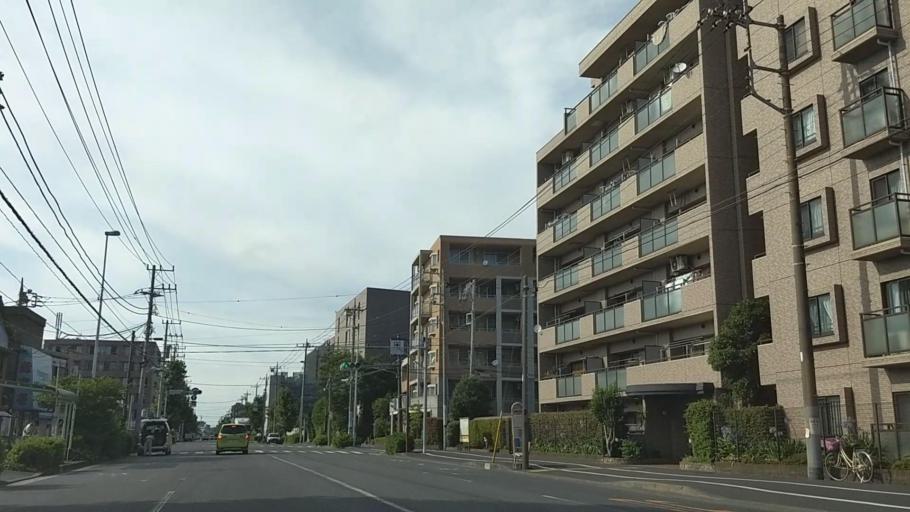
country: JP
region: Kanagawa
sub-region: Kawasaki-shi
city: Kawasaki
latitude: 35.5045
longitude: 139.6937
